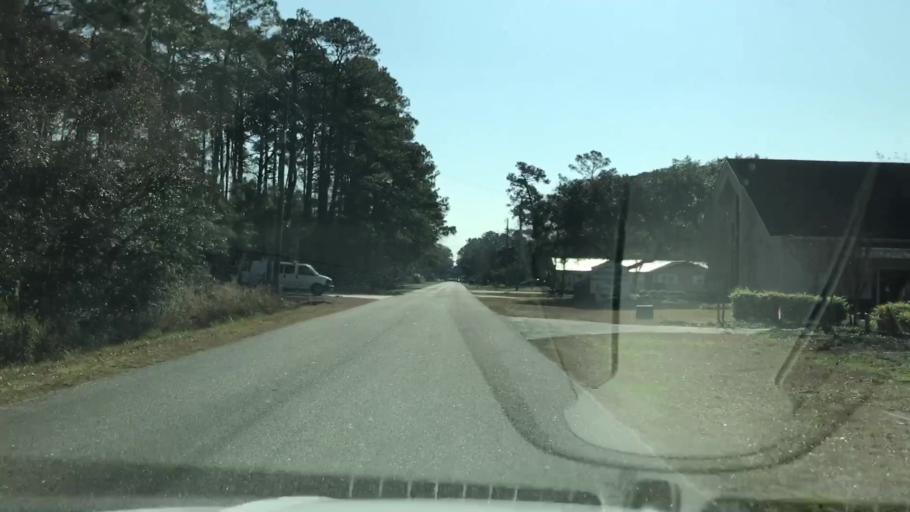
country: US
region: South Carolina
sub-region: Horry County
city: Garden City
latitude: 33.5869
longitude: -79.0053
